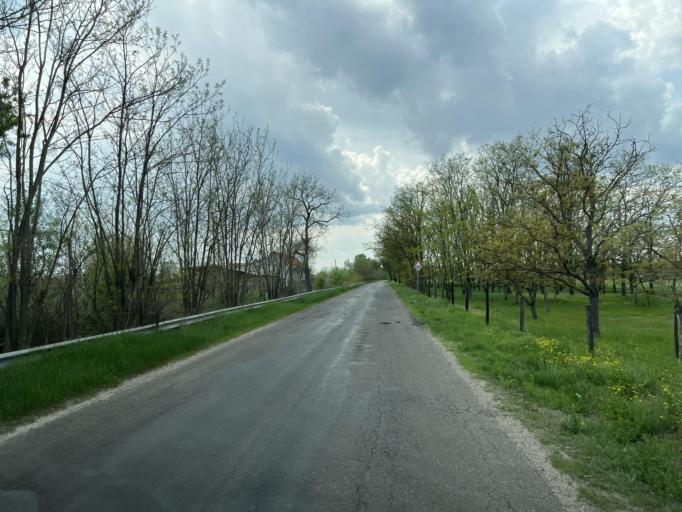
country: HU
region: Pest
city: Cegled
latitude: 47.1339
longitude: 19.7791
